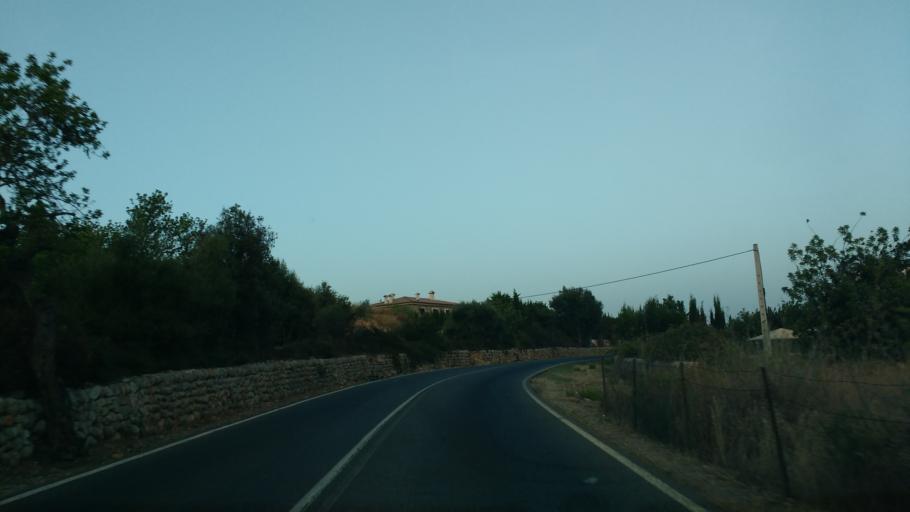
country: ES
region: Balearic Islands
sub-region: Illes Balears
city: Bunyola
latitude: 39.6672
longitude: 2.6868
